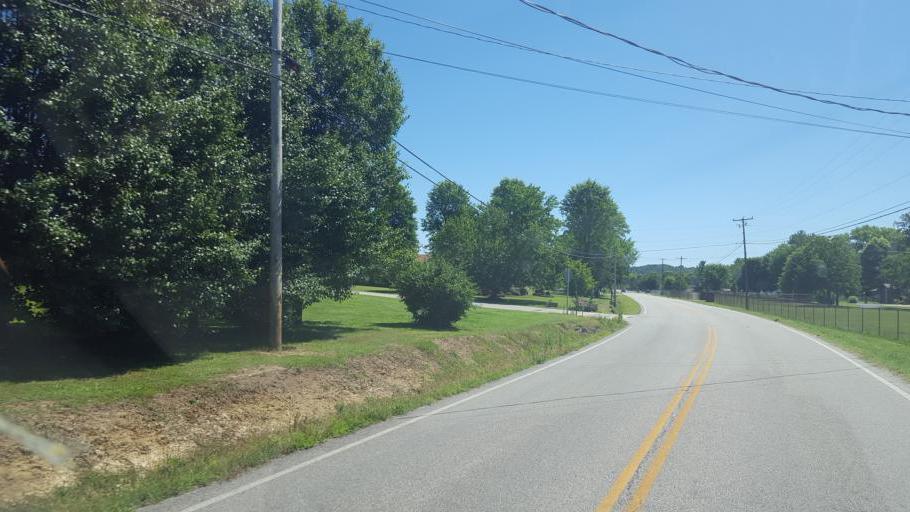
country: US
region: West Virginia
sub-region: Cabell County
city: Pea Ridge
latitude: 38.4432
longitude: -82.3402
